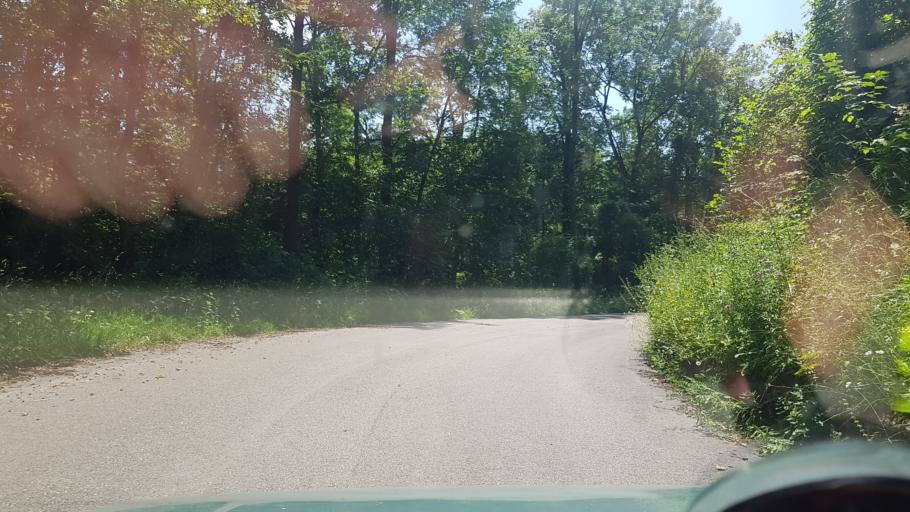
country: IT
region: Friuli Venezia Giulia
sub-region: Provincia di Udine
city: Lusevera
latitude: 46.2709
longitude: 13.2916
